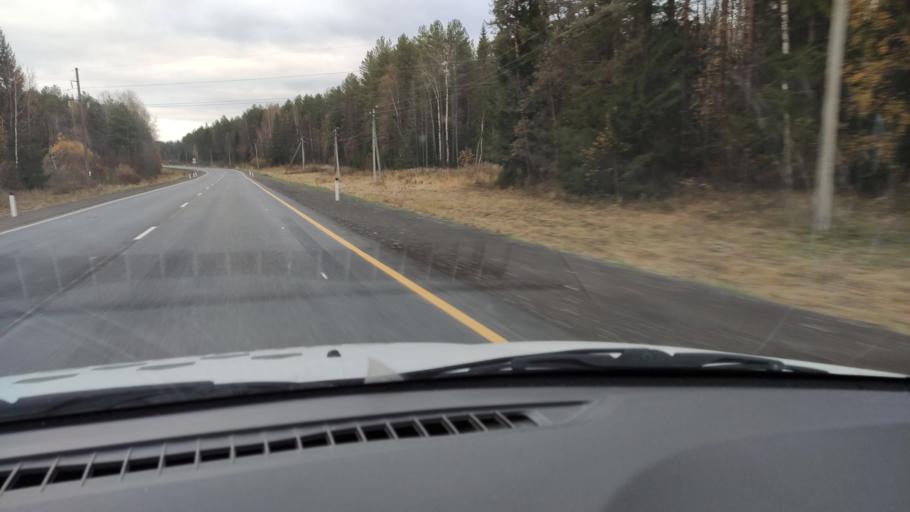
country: RU
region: Kirov
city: Belaya Kholunitsa
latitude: 58.8458
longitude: 50.7635
